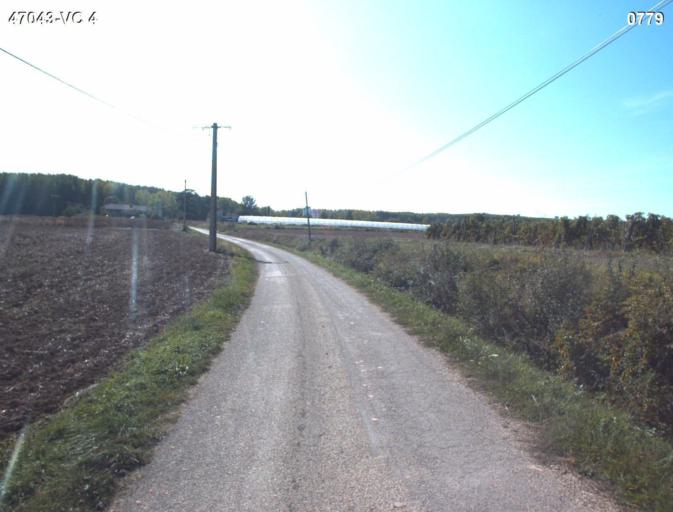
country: FR
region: Aquitaine
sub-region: Departement du Lot-et-Garonne
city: Buzet-sur-Baise
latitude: 44.2638
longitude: 0.3120
